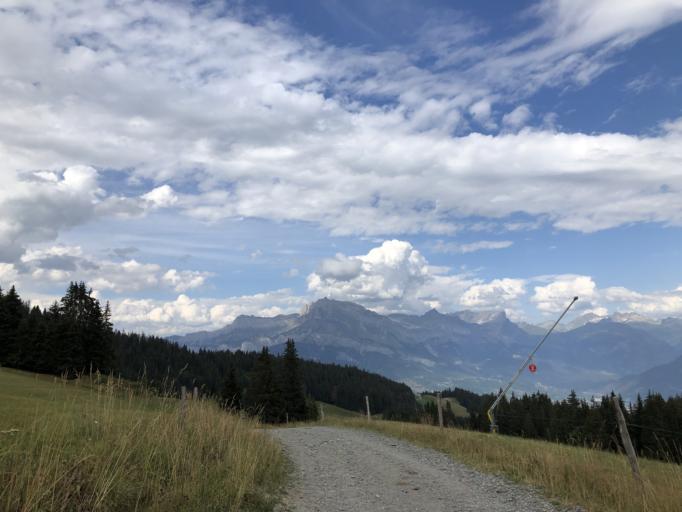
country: FR
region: Rhone-Alpes
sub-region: Departement de la Haute-Savoie
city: Megeve
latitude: 45.8721
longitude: 6.5999
